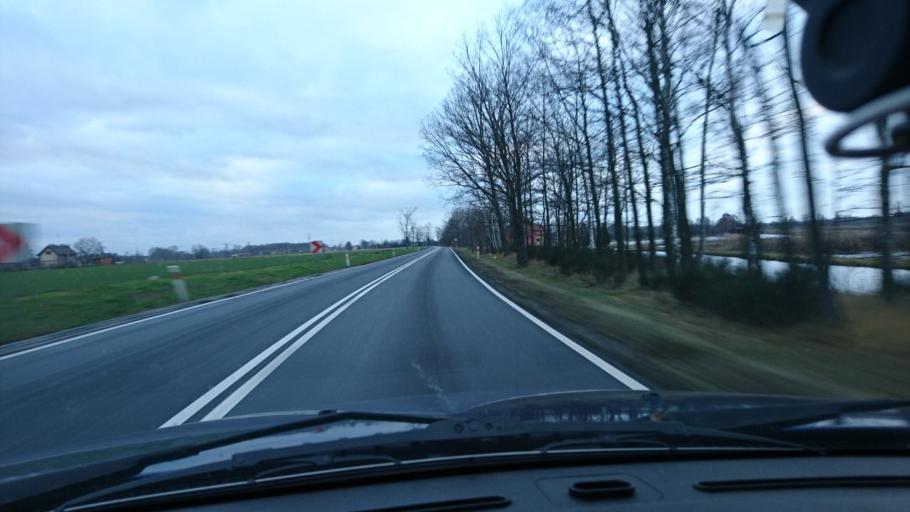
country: PL
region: Lodz Voivodeship
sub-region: Powiat wieruszowski
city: Boleslawiec
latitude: 51.1570
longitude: 18.1692
